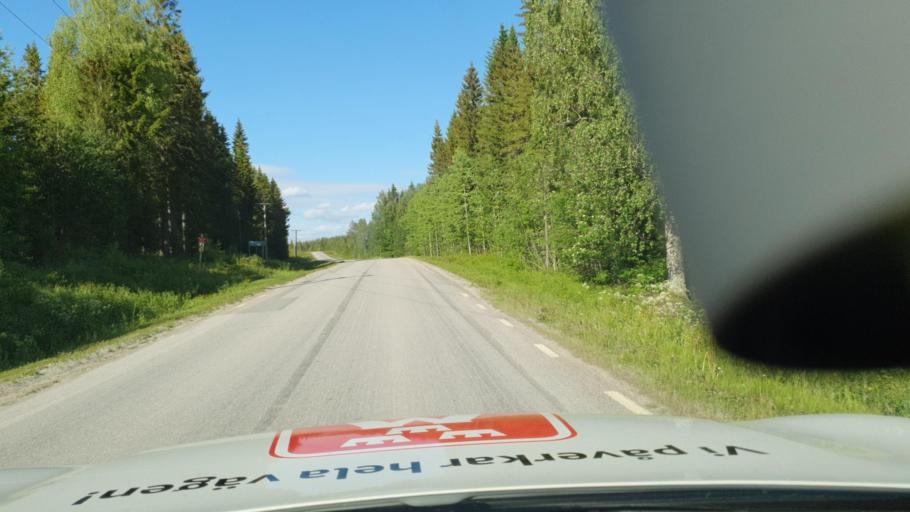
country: SE
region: Vaesterbotten
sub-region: Vannas Kommun
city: Vaennaes
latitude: 63.8708
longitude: 19.6760
